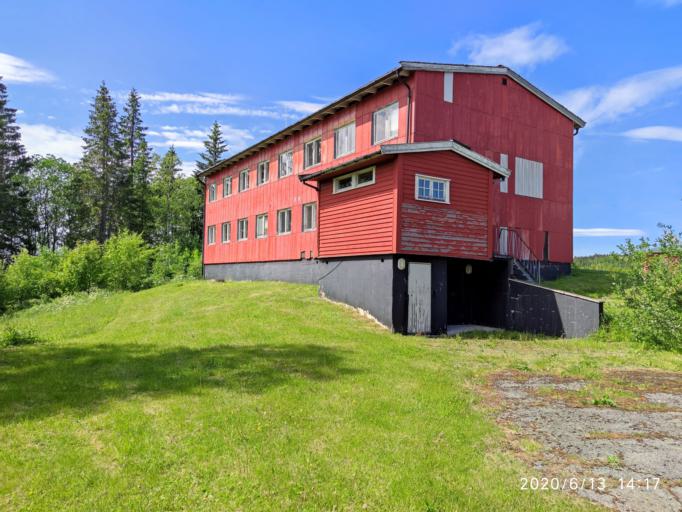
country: NO
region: Akershus
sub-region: Asker
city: Asker
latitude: 59.8772
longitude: 10.3786
